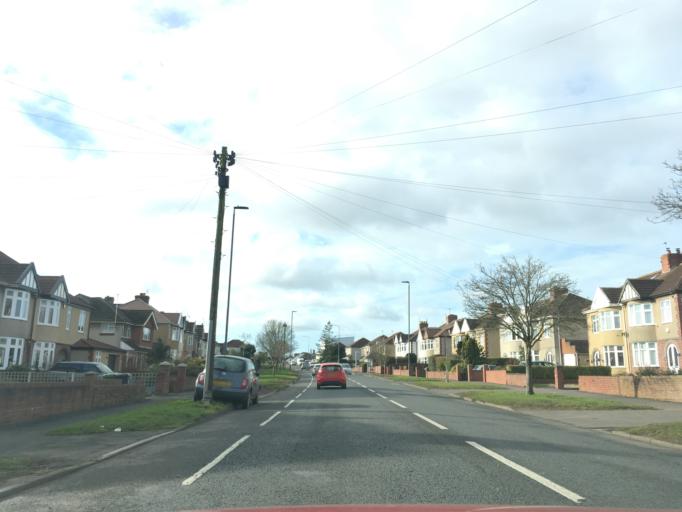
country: GB
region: England
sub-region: South Gloucestershire
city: Mangotsfield
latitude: 51.4971
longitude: -2.4989
